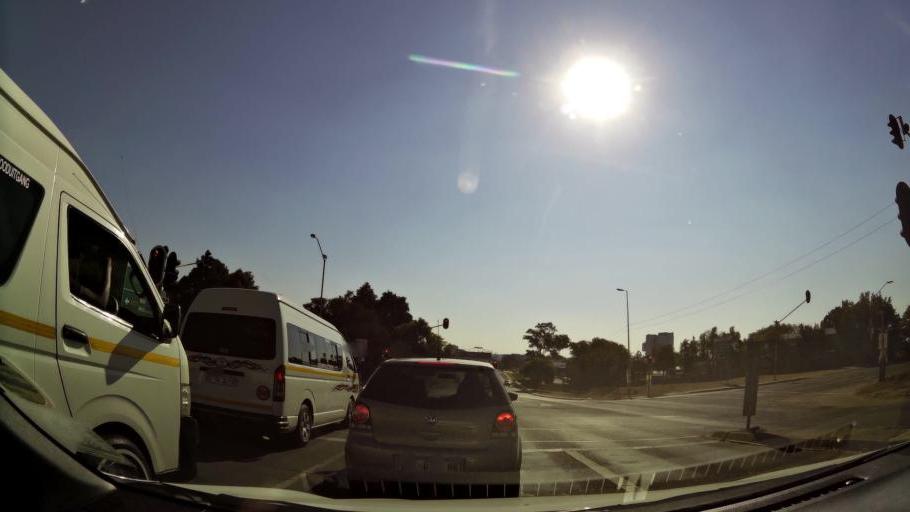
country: ZA
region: Gauteng
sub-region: City of Tshwane Metropolitan Municipality
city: Pretoria
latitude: -25.7950
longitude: 28.2840
